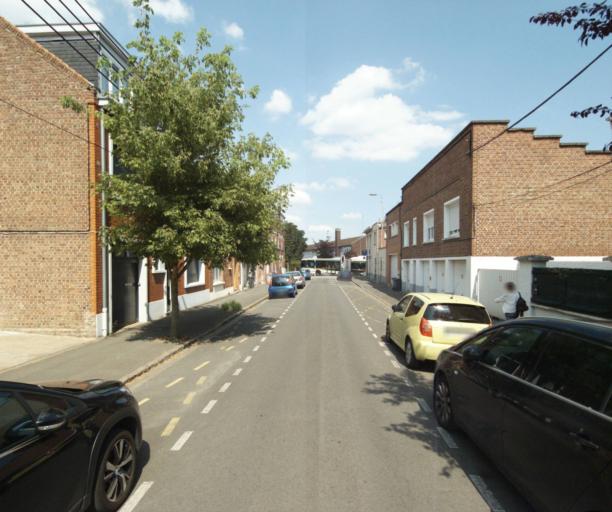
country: FR
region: Nord-Pas-de-Calais
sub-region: Departement du Nord
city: Saint-Andre-lez-Lille
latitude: 50.6632
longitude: 3.0493
